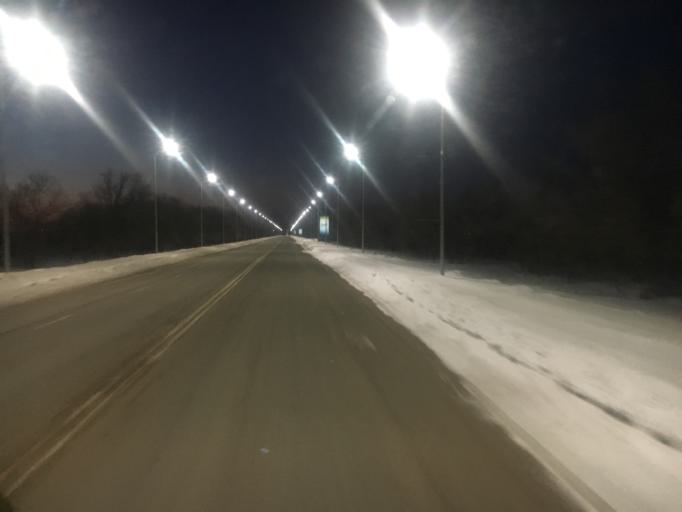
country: KZ
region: Batys Qazaqstan
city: Oral
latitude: 51.1564
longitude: 51.5351
